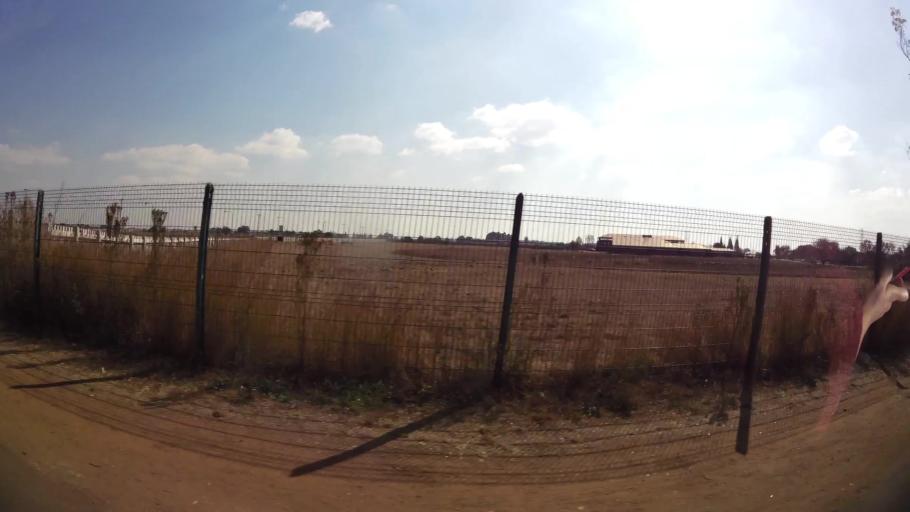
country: ZA
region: Gauteng
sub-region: Ekurhuleni Metropolitan Municipality
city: Benoni
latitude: -26.1452
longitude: 28.3966
